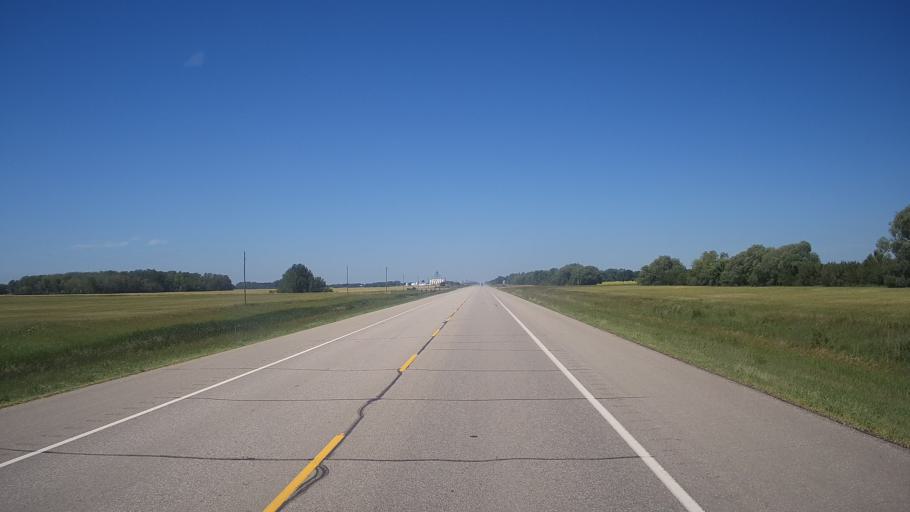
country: CA
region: Manitoba
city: Neepawa
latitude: 50.2257
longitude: -99.0146
